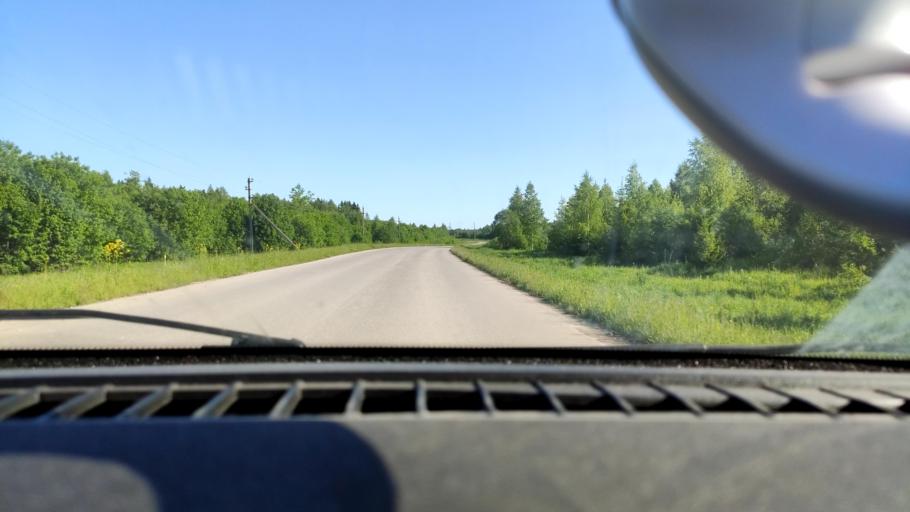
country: RU
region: Perm
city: Polazna
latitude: 58.2010
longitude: 56.5316
